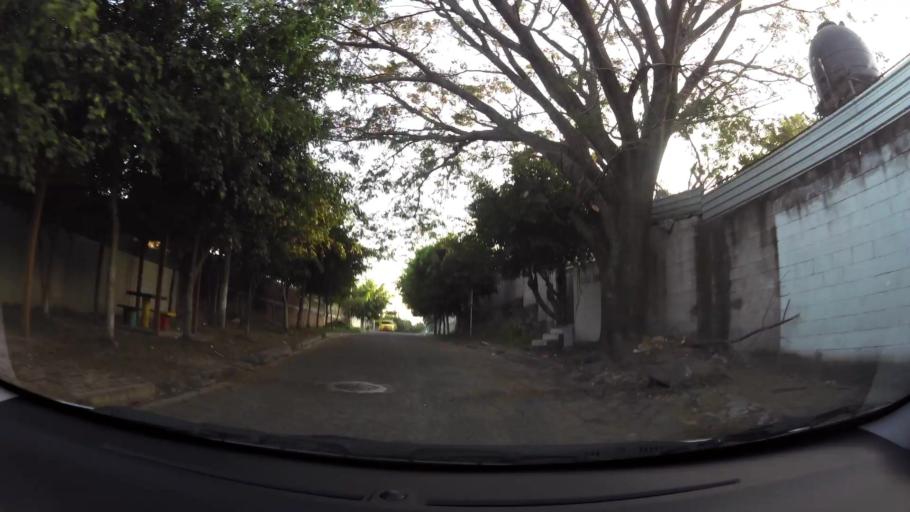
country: SV
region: San Salvador
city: Cuscatancingo
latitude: 13.7178
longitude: -89.1944
